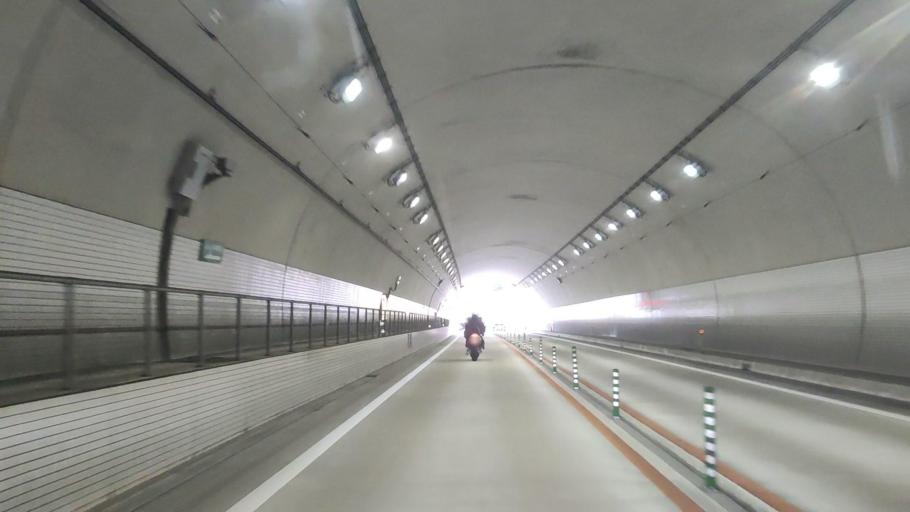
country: JP
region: Shizuoka
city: Ito
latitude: 34.9489
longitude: 138.9452
